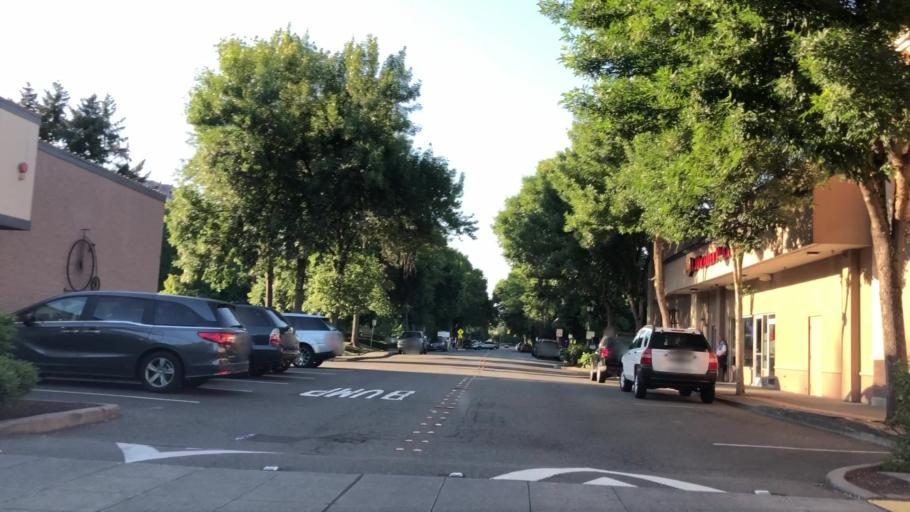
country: US
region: Washington
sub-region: King County
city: Redmond
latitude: 47.6756
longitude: -122.1303
